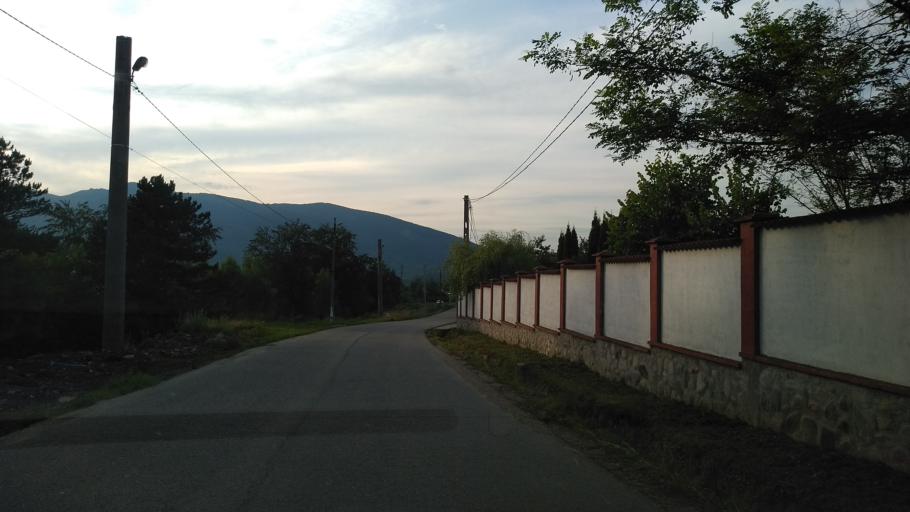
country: RO
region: Hunedoara
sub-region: Municipiul  Vulcan
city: Jiu-Paroseni
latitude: 45.3563
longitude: 23.2893
